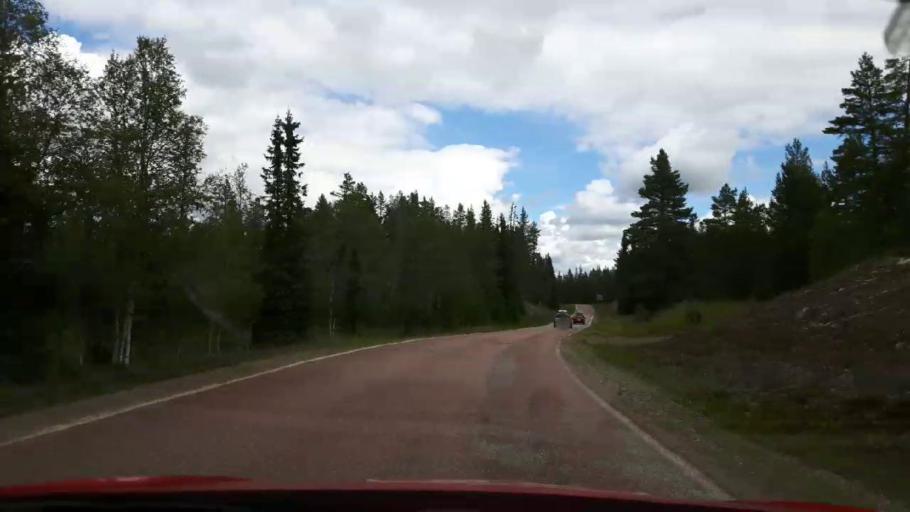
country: NO
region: Hedmark
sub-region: Trysil
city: Innbygda
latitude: 61.8607
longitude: 12.9481
